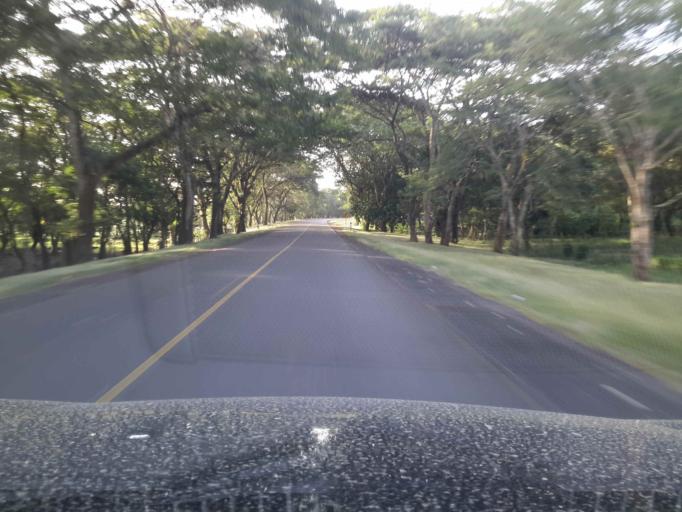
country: NI
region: Rio San Juan
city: San Miguelito
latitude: 11.4007
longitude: -84.8269
